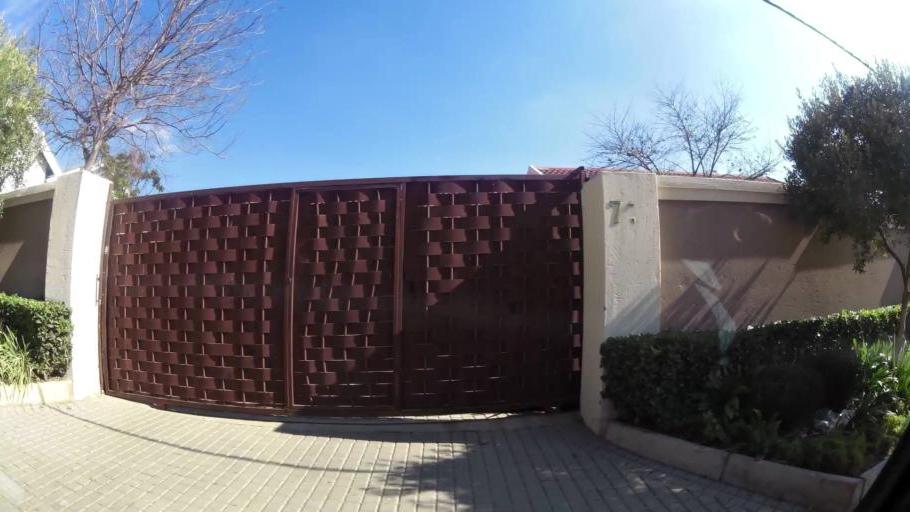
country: ZA
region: Gauteng
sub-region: West Rand District Municipality
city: Muldersdriseloop
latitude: -26.0146
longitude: 27.9350
